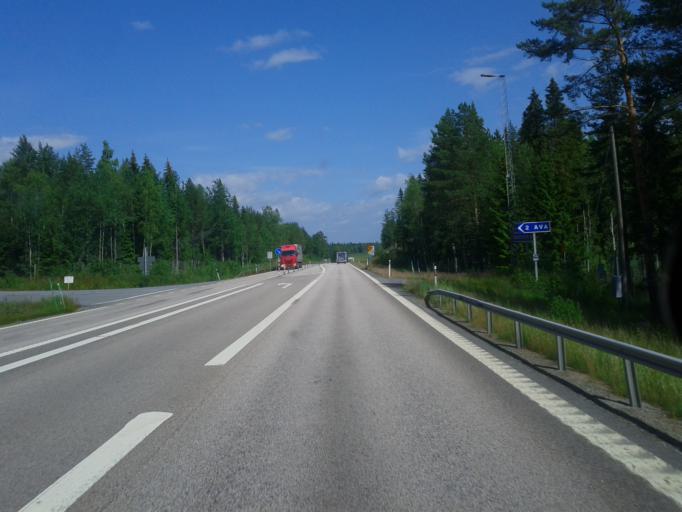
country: SE
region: Vaesterbotten
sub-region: Nordmalings Kommun
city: Nordmaling
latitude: 63.4942
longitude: 19.3197
